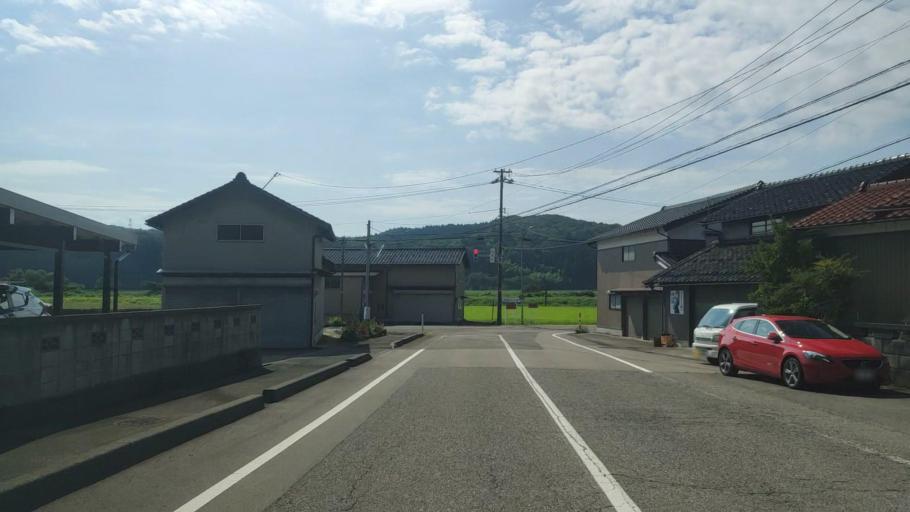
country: JP
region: Ishikawa
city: Komatsu
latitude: 36.3807
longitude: 136.4972
